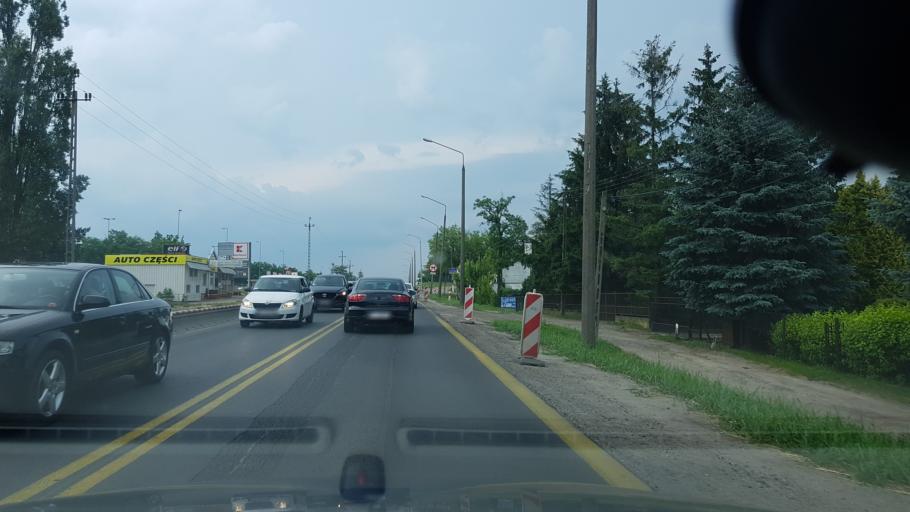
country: PL
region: Masovian Voivodeship
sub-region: Powiat legionowski
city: Michalow-Reginow
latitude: 52.4067
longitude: 20.9530
